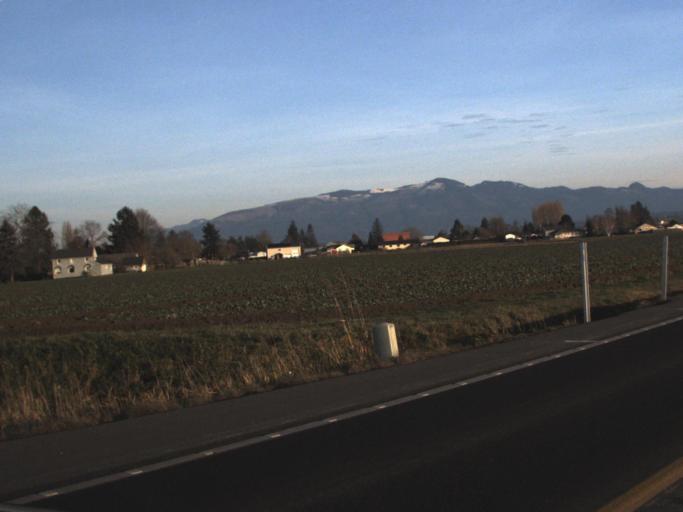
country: US
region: Washington
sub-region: Skagit County
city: Mount Vernon
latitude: 48.4416
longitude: -122.3886
